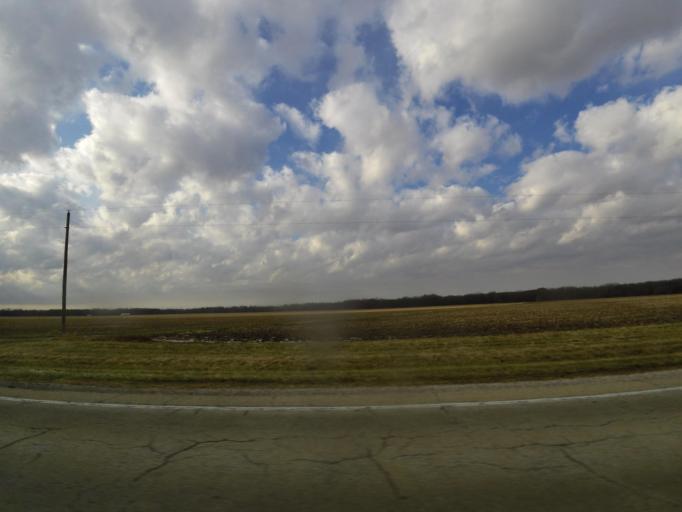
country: US
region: Illinois
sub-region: Fayette County
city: Ramsey
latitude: 39.1880
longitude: -89.0987
